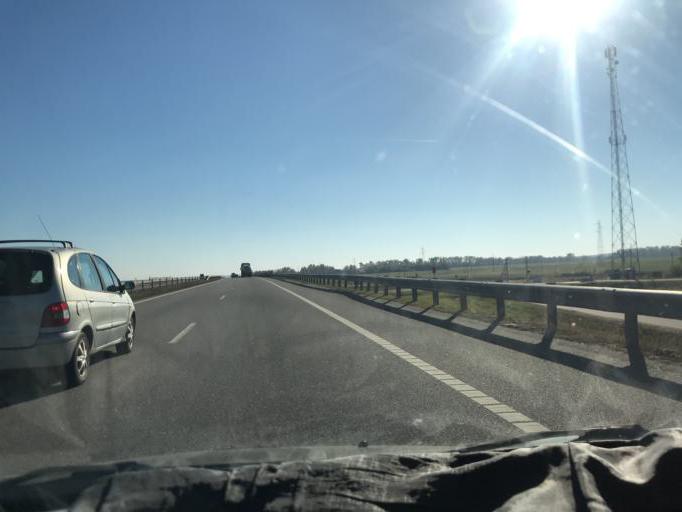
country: BY
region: Mogilev
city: Yalizava
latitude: 53.2481
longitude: 28.9309
